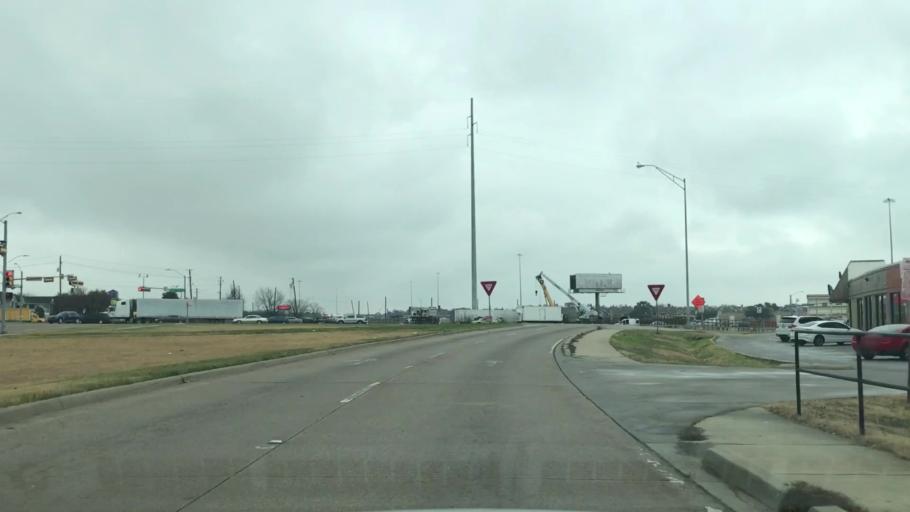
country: US
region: Texas
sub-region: Dallas County
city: Richardson
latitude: 32.9031
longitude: -96.7174
